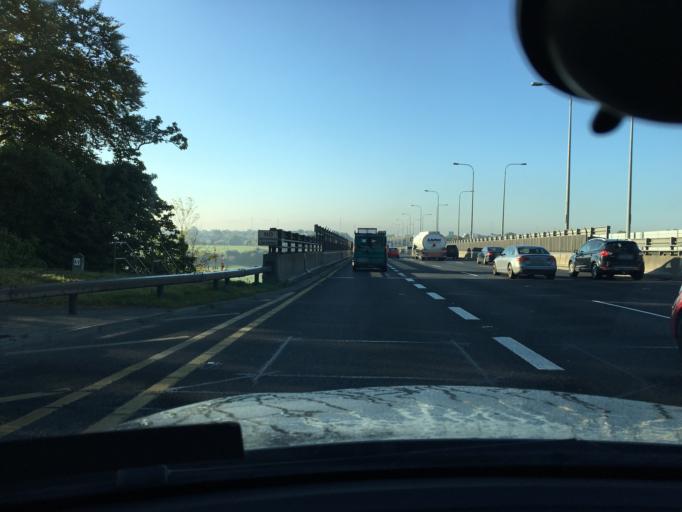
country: IE
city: Palmerstown
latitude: 53.3638
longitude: -6.3819
